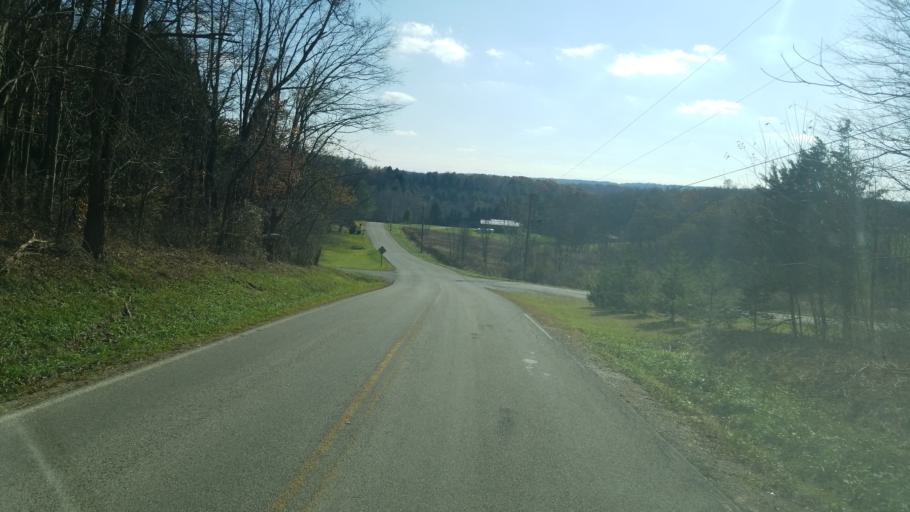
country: US
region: Ohio
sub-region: Sandusky County
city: Bellville
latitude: 40.6242
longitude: -82.4444
